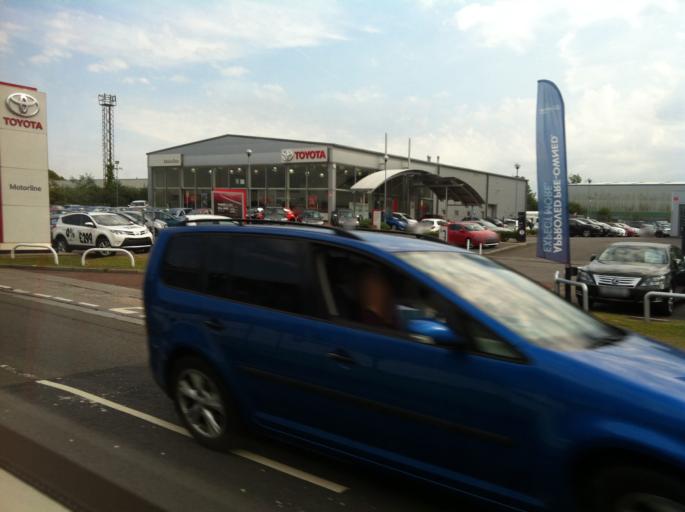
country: GB
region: Wales
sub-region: Cardiff
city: Cardiff
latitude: 51.4649
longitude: -3.1965
